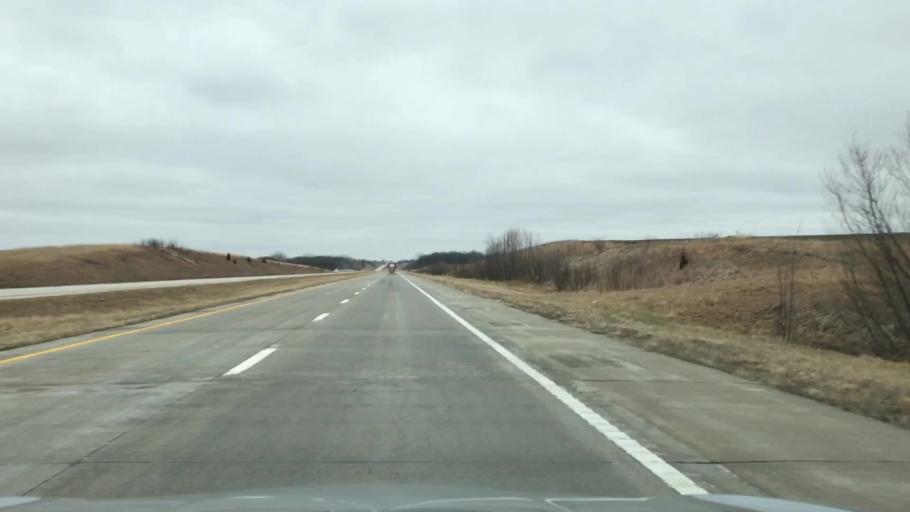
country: US
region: Missouri
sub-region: Caldwell County
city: Hamilton
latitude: 39.7339
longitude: -93.9806
